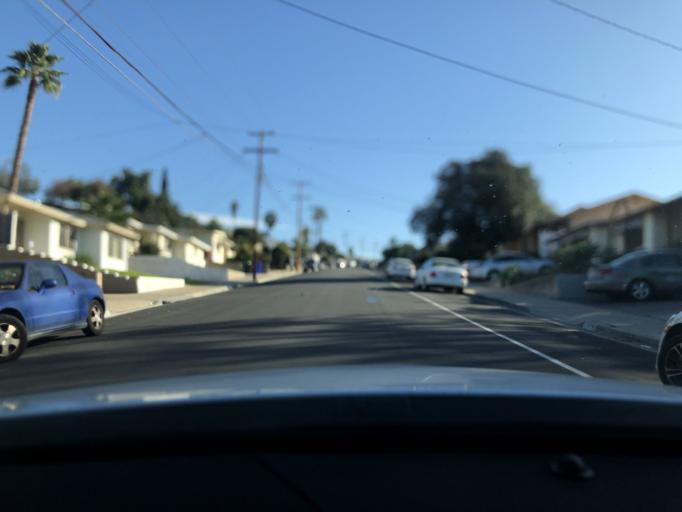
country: US
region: California
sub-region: San Diego County
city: Lemon Grove
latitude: 32.7509
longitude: -117.0652
